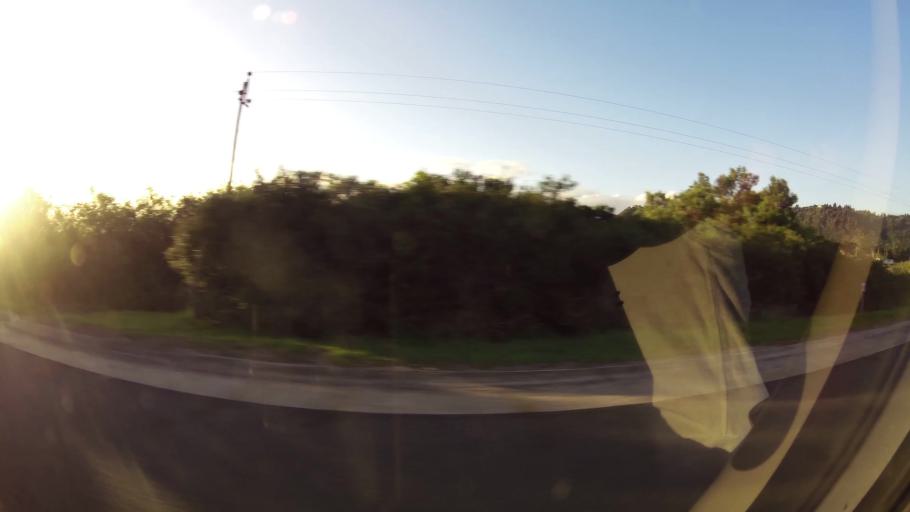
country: ZA
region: Western Cape
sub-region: Eden District Municipality
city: Knysna
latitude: -34.0093
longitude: 22.7717
